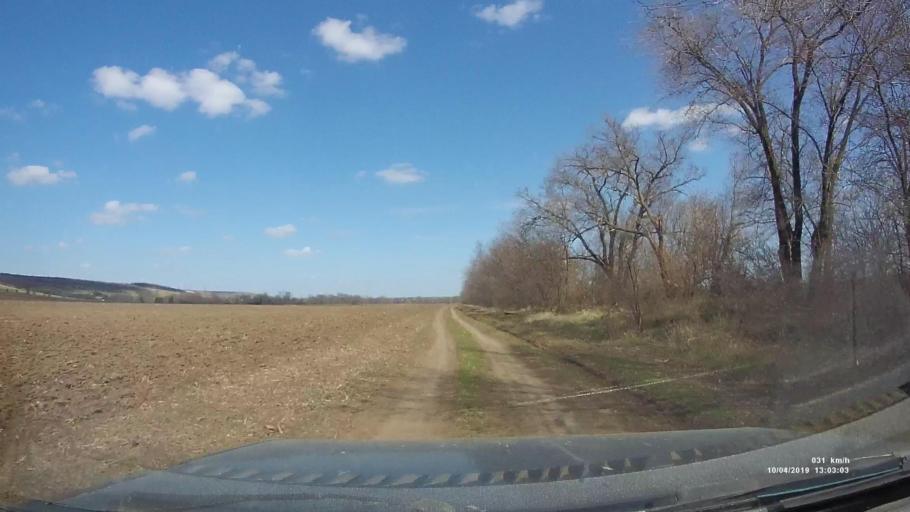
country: RU
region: Rostov
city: Masalovka
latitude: 48.3822
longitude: 40.2319
